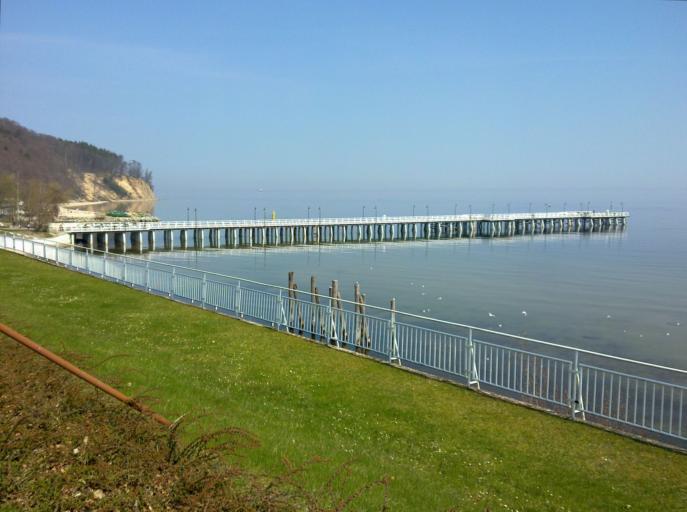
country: PL
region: Pomeranian Voivodeship
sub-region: Sopot
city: Sopot
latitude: 54.4788
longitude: 18.5634
